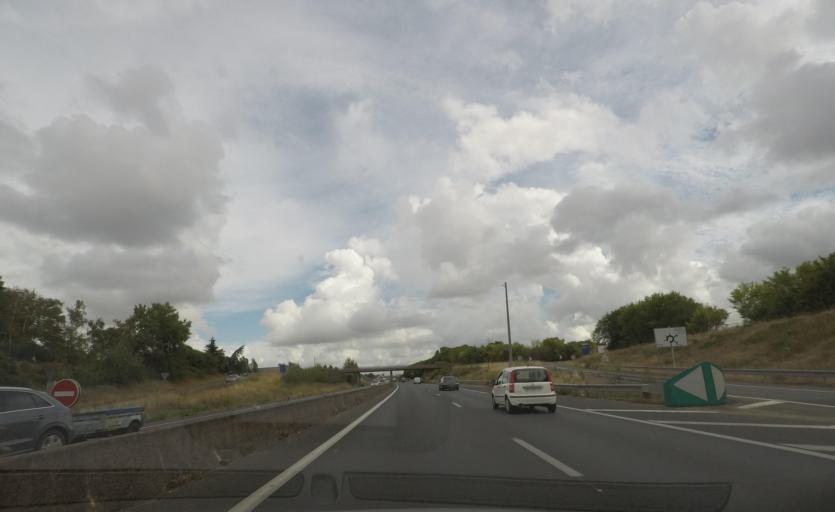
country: FR
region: Pays de la Loire
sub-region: Departement de Maine-et-Loire
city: Trelaze
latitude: 47.4813
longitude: -0.4992
